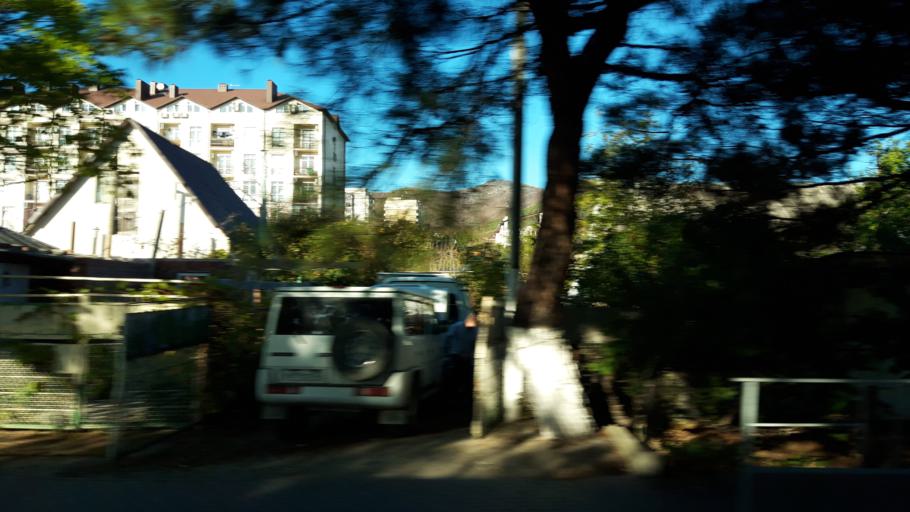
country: RU
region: Krasnodarskiy
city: Kabardinka
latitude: 44.6499
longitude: 37.9448
